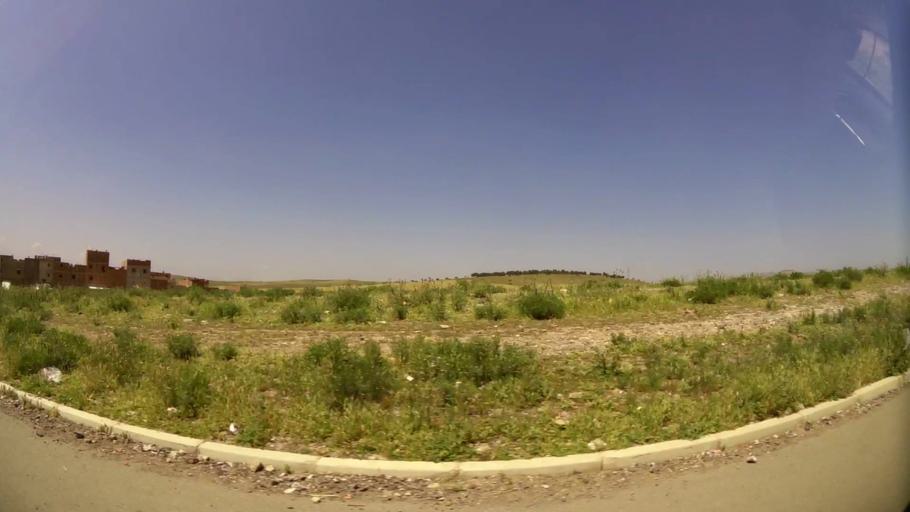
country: MA
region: Oriental
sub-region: Oujda-Angad
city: Oujda
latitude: 34.6805
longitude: -1.9602
